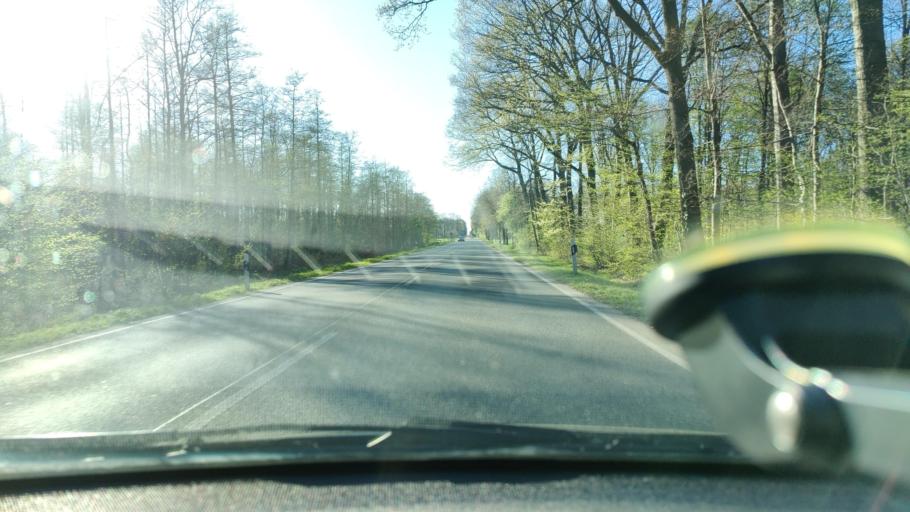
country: DE
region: North Rhine-Westphalia
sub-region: Regierungsbezirk Munster
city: Legden
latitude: 52.0523
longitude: 7.0582
